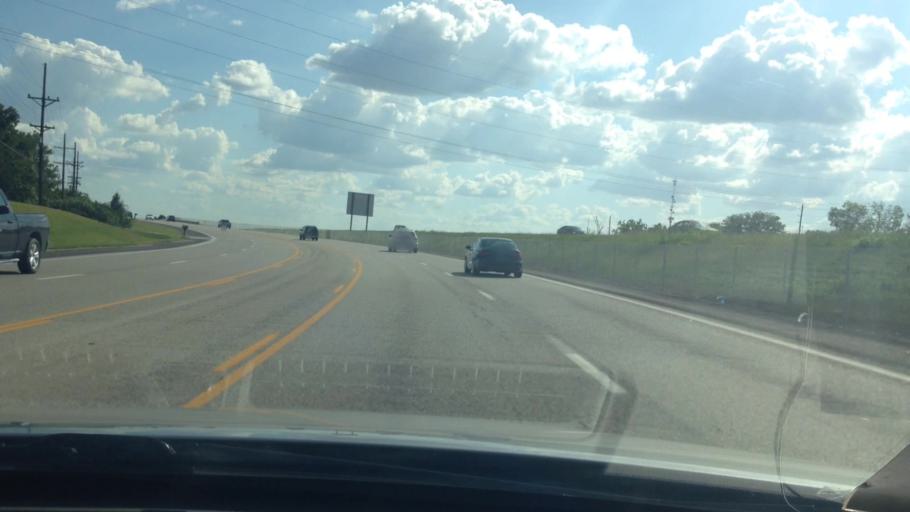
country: US
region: Missouri
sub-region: Clay County
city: Liberty
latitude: 39.2599
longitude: -94.4487
